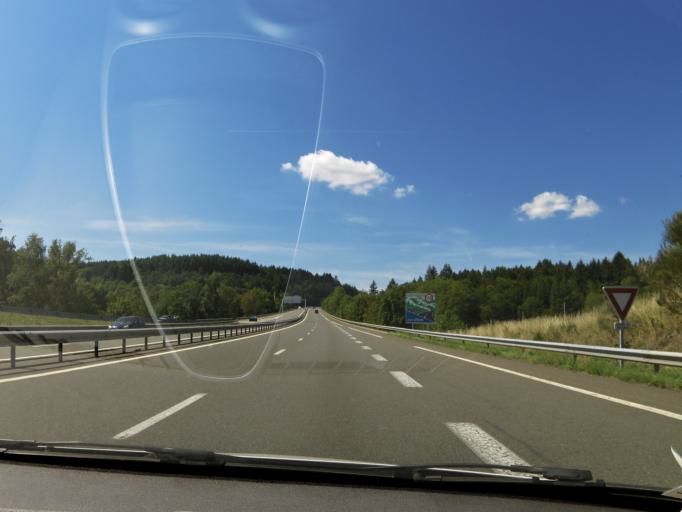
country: FR
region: Rhone-Alpes
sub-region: Departement de la Loire
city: Noiretable
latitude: 45.8533
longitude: 3.7899
